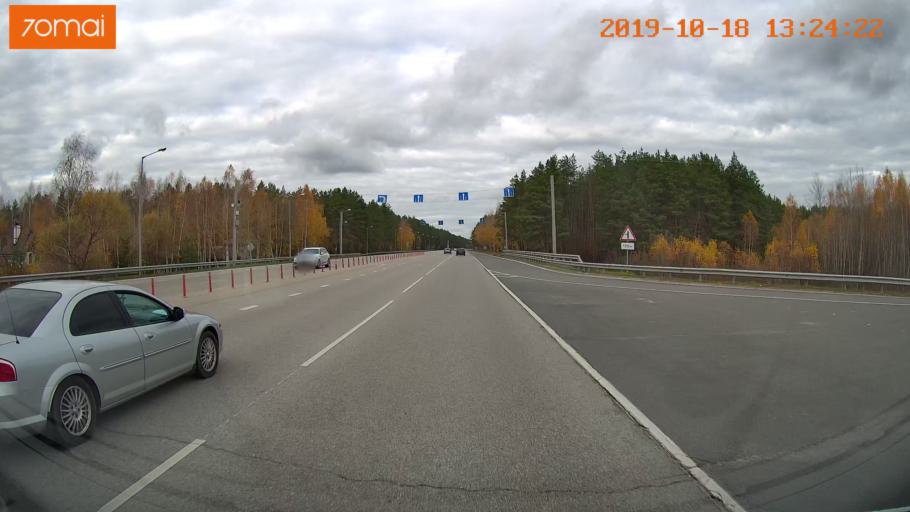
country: RU
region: Rjazan
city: Polyany
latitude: 54.7298
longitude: 39.8443
